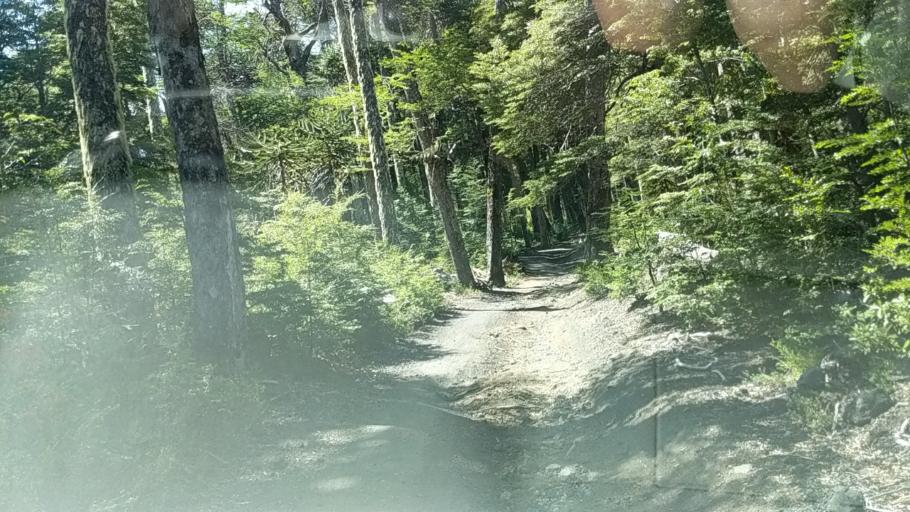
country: CL
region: Araucania
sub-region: Provincia de Cautin
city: Pucon
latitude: -39.4646
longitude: -71.8519
